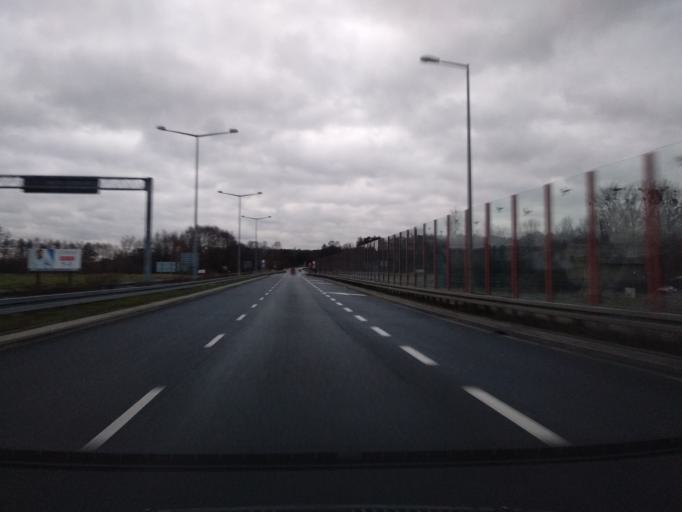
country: PL
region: Greater Poland Voivodeship
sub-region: Powiat koninski
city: Stare Miasto
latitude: 52.1776
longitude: 18.2210
